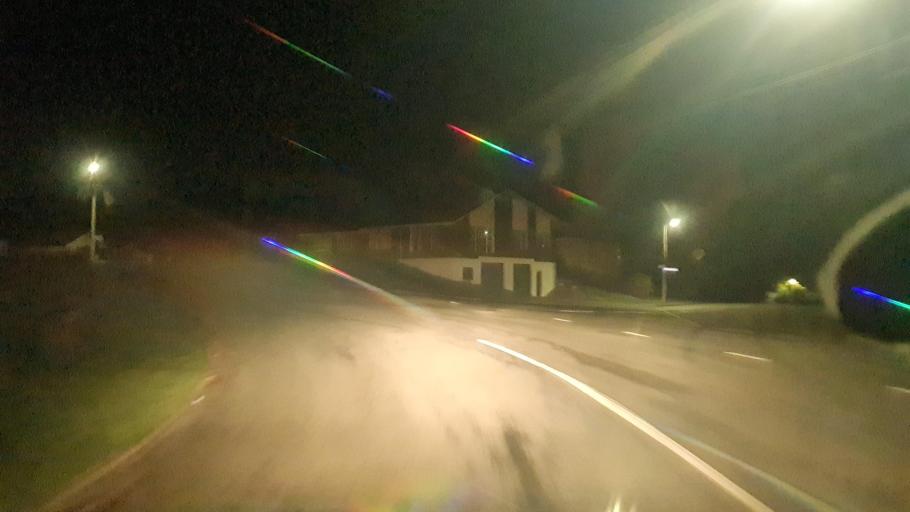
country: NZ
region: Otago
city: Oamaru
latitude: -45.0805
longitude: 170.9711
